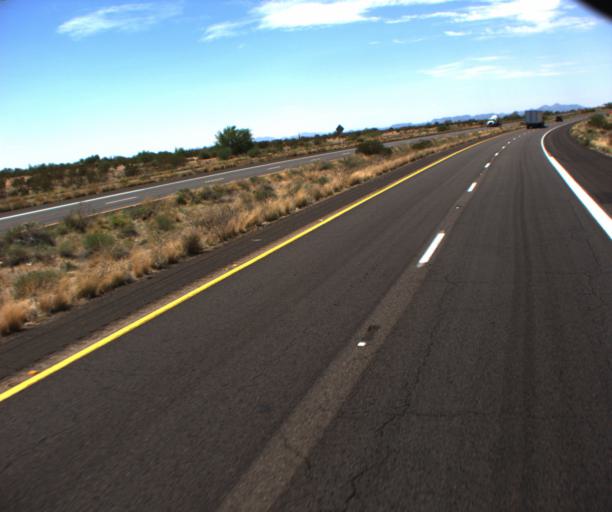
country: US
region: Arizona
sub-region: Pinal County
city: Gold Camp
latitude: 33.2560
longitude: -111.3303
